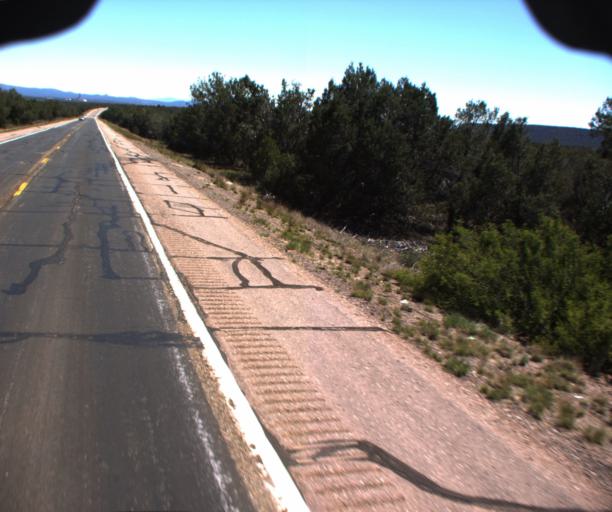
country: US
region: Arizona
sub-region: Yavapai County
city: Paulden
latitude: 35.0585
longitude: -112.3983
